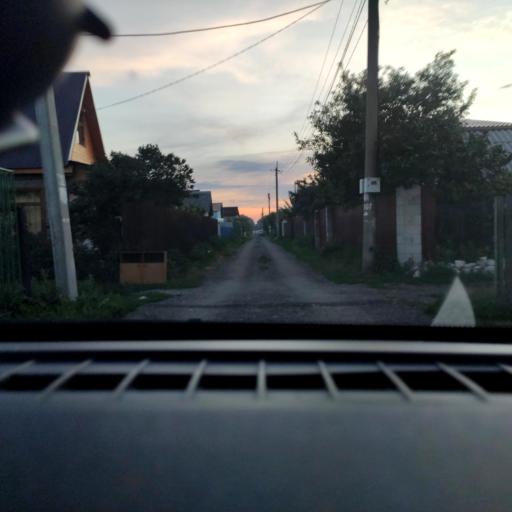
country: RU
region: Samara
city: Tol'yatti
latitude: 53.6315
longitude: 49.4129
